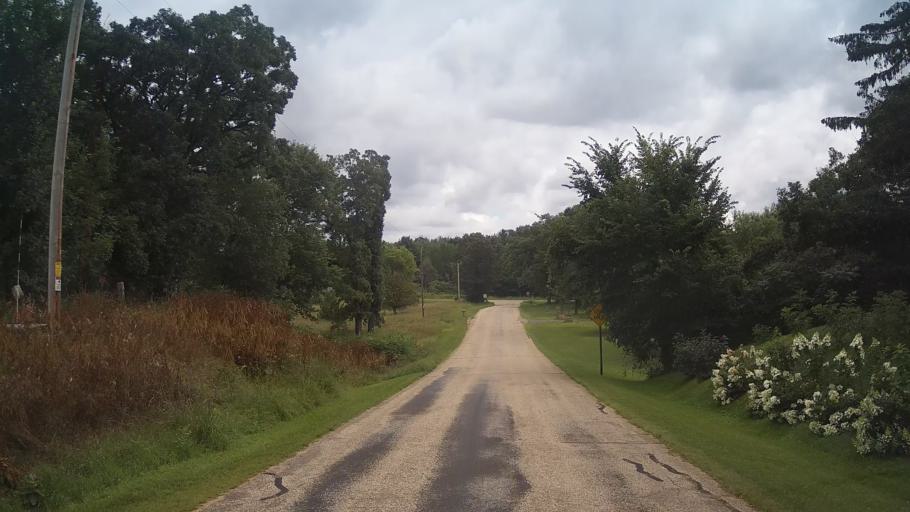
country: US
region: Wisconsin
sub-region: Adams County
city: Friendship
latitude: 44.0327
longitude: -89.8909
